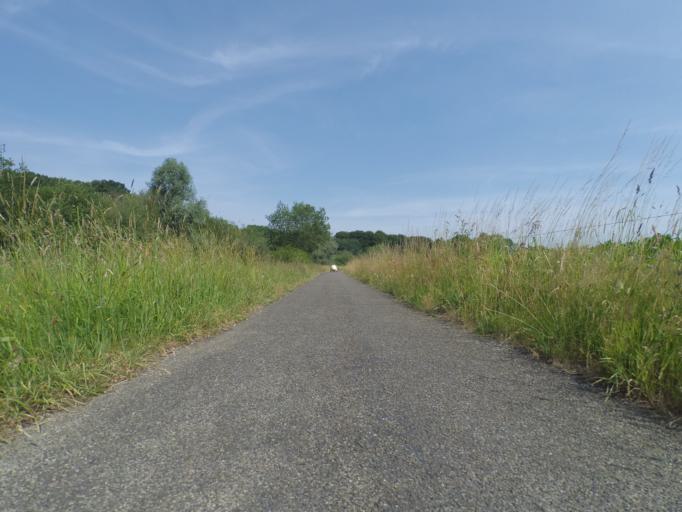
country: NL
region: North Brabant
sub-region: Gemeente Breda
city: Breda
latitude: 51.5422
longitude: 4.7805
